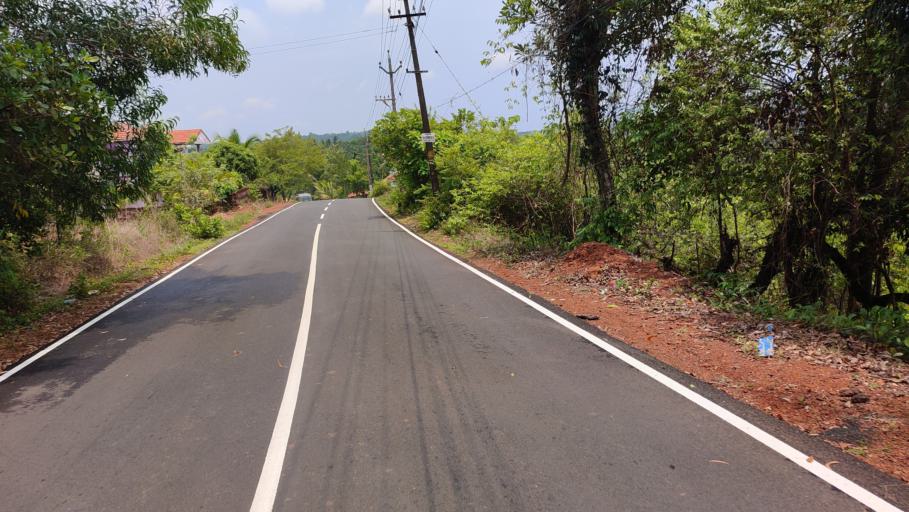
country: IN
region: Kerala
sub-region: Kasaragod District
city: Kannangad
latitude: 12.3196
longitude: 75.1370
